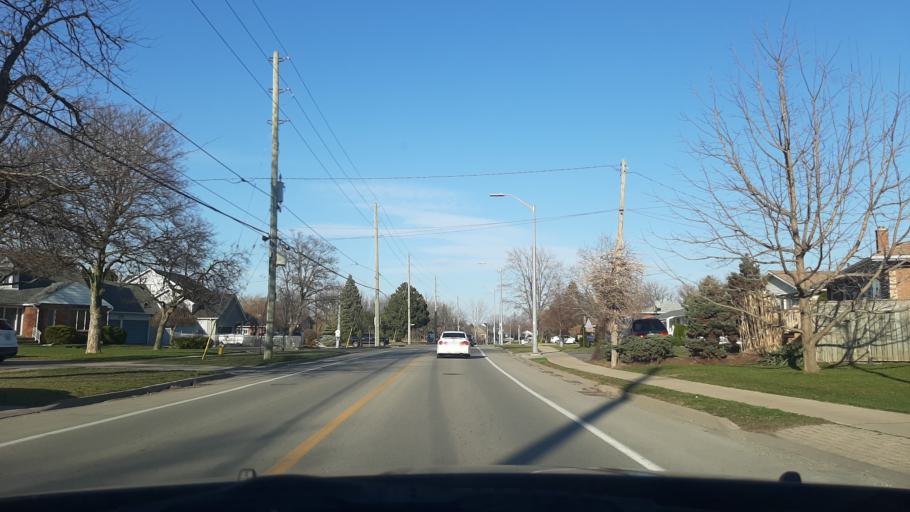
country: CA
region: Ontario
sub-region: Regional Municipality of Niagara
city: St. Catharines
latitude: 43.2113
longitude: -79.2292
